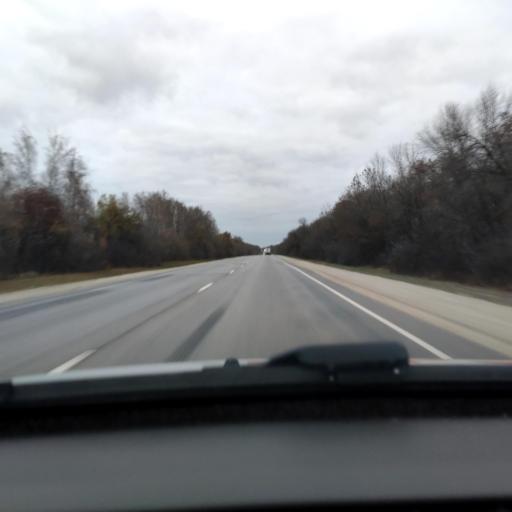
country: RU
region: Lipetsk
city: Borinskoye
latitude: 52.3783
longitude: 39.2165
